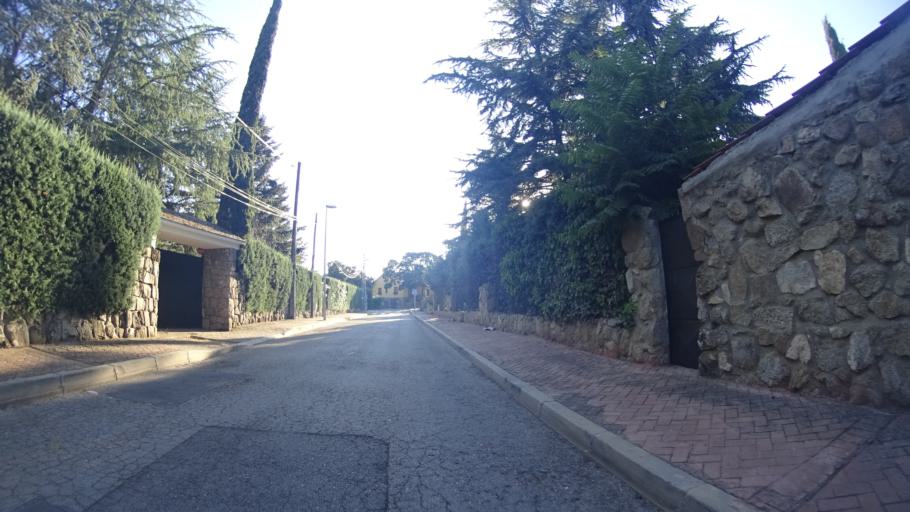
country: ES
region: Madrid
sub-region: Provincia de Madrid
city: Galapagar
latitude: 40.5668
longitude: -4.0013
